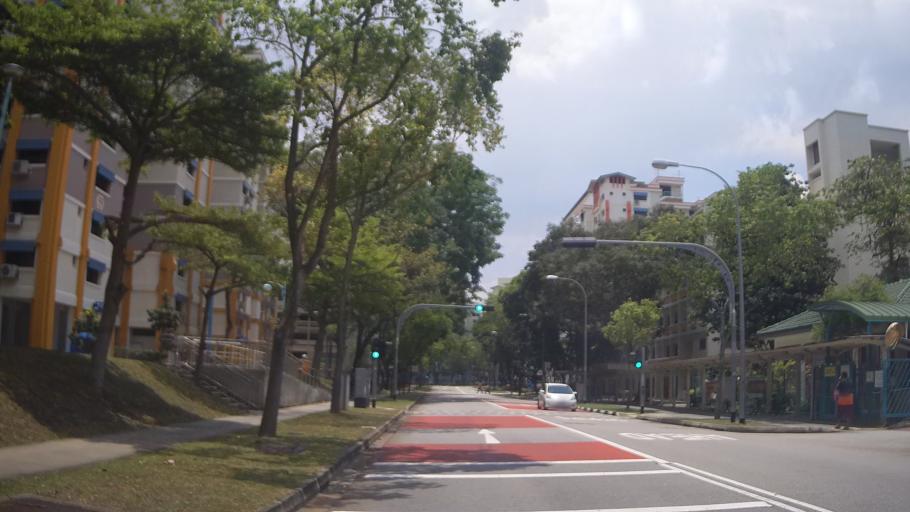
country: MY
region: Johor
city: Johor Bahru
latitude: 1.4441
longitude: 103.7954
